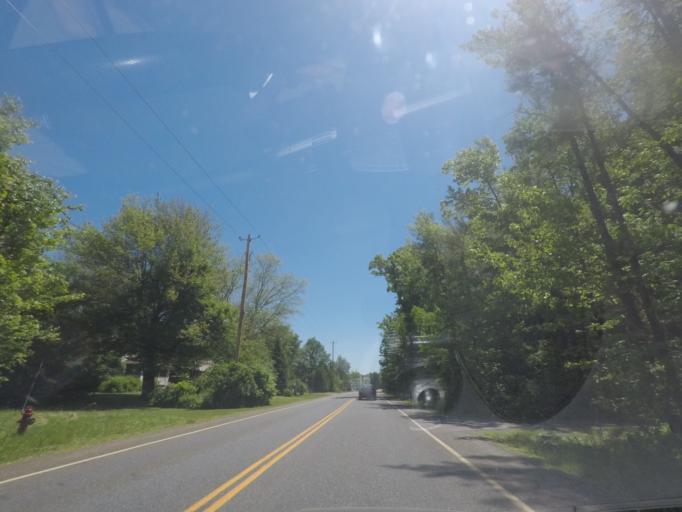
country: US
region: New York
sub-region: Saratoga County
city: Mechanicville
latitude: 42.9461
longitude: -73.7135
